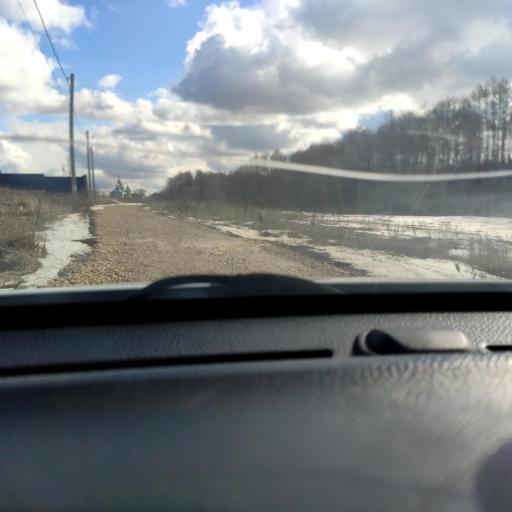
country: RU
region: Voronezj
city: Novaya Usman'
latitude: 51.6860
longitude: 39.3889
